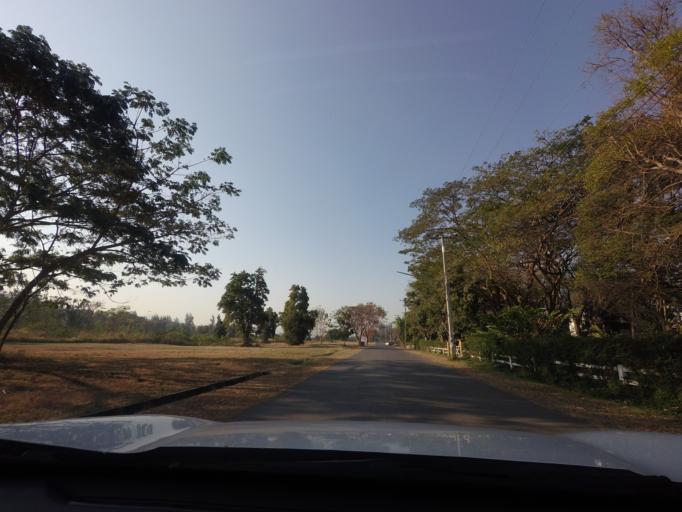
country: TH
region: Nakhon Ratchasima
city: Pak Chong
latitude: 14.5851
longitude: 101.4477
